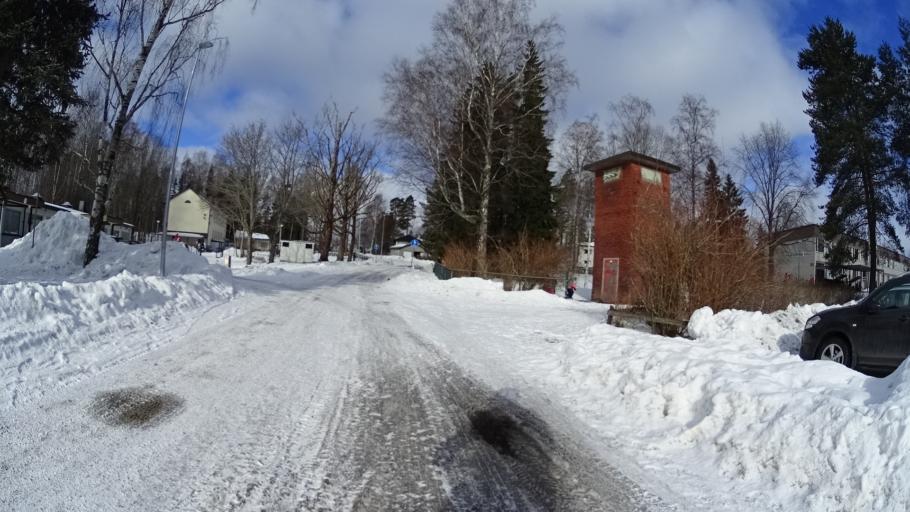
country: FI
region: Uusimaa
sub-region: Helsinki
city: Kilo
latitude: 60.2578
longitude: 24.8235
